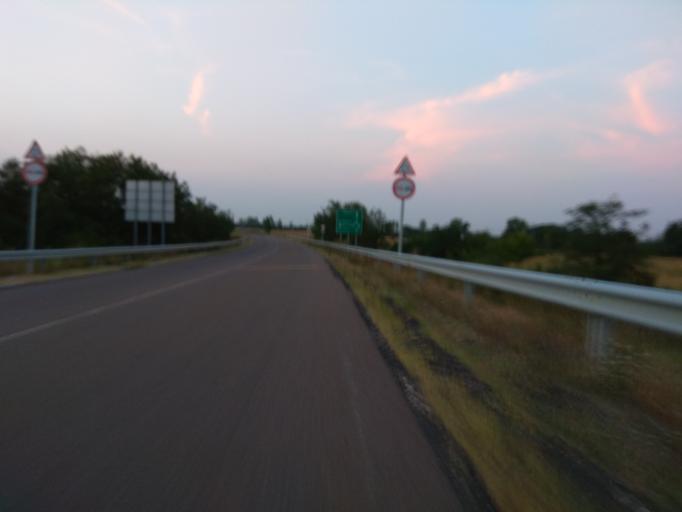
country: HU
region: Borsod-Abauj-Zemplen
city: Emod
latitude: 47.9407
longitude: 20.8298
